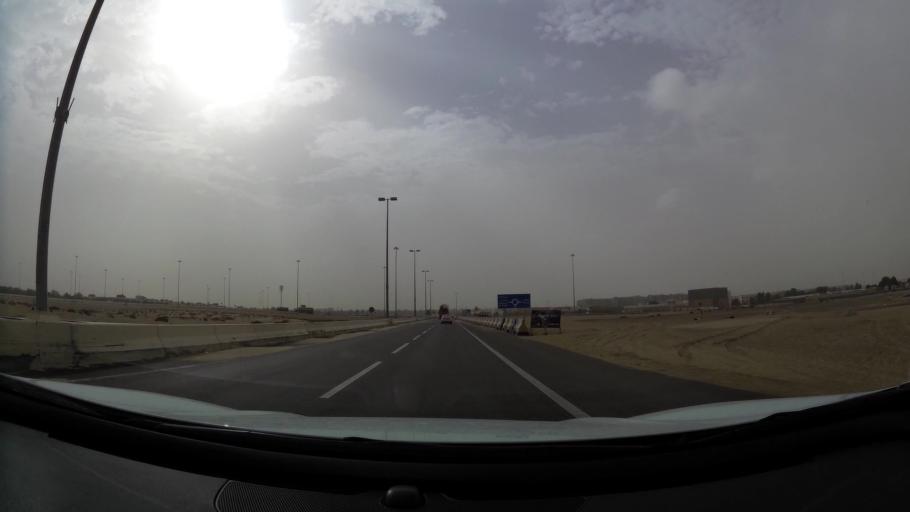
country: AE
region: Abu Dhabi
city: Abu Dhabi
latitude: 24.4659
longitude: 54.6734
